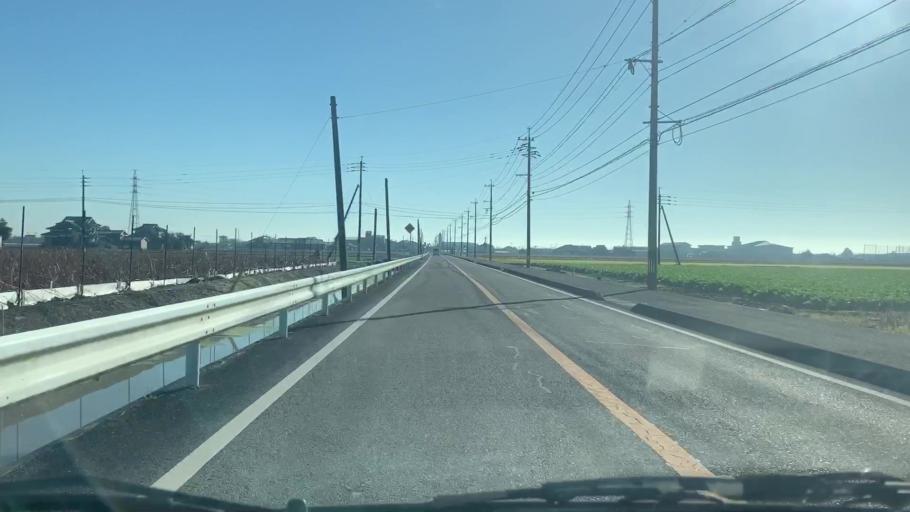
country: JP
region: Saga Prefecture
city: Kashima
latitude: 33.1922
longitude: 130.1245
